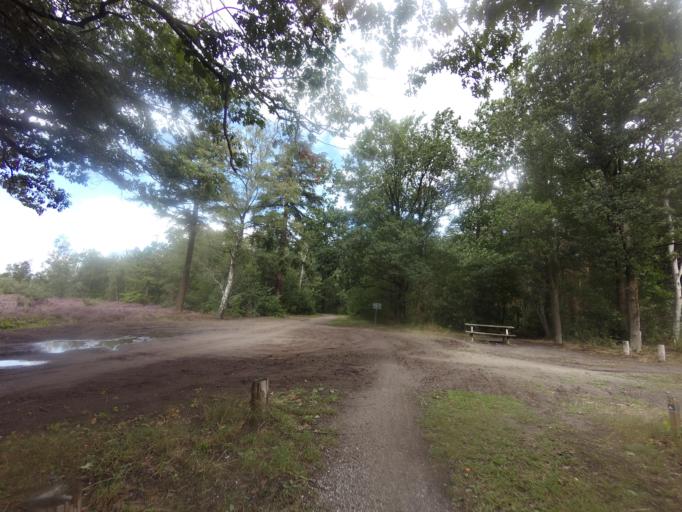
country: NL
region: Overijssel
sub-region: Gemeente Staphorst
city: Staphorst
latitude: 52.6460
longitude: 6.2665
